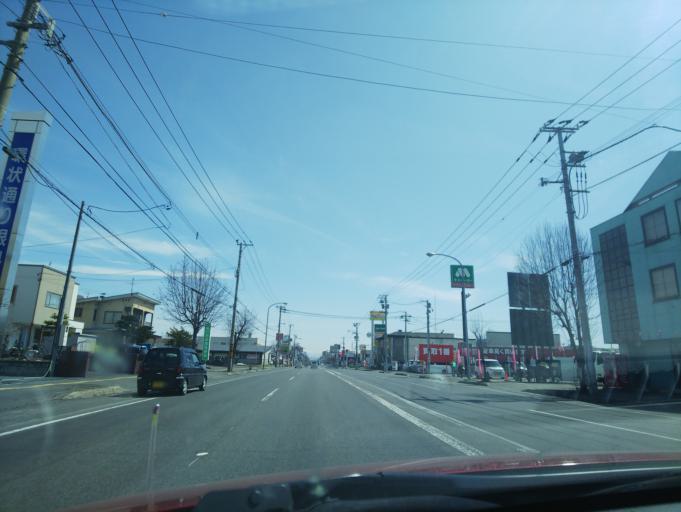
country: JP
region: Hokkaido
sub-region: Asahikawa-shi
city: Asahikawa
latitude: 43.7902
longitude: 142.4053
